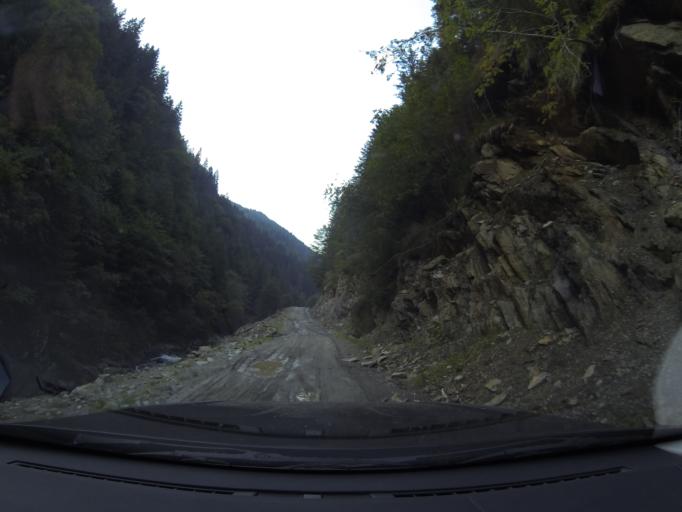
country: RO
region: Brasov
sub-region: Oras Victoria
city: Victoria
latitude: 45.5356
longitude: 24.6779
